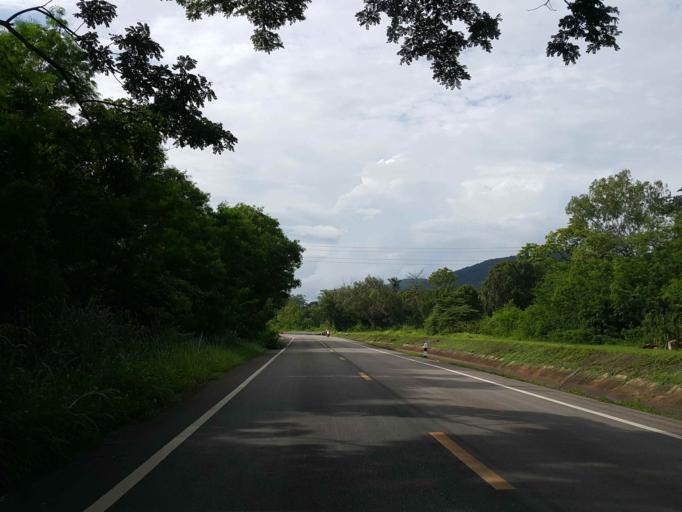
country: TH
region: Chiang Mai
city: San Sai
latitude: 18.9153
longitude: 99.1485
